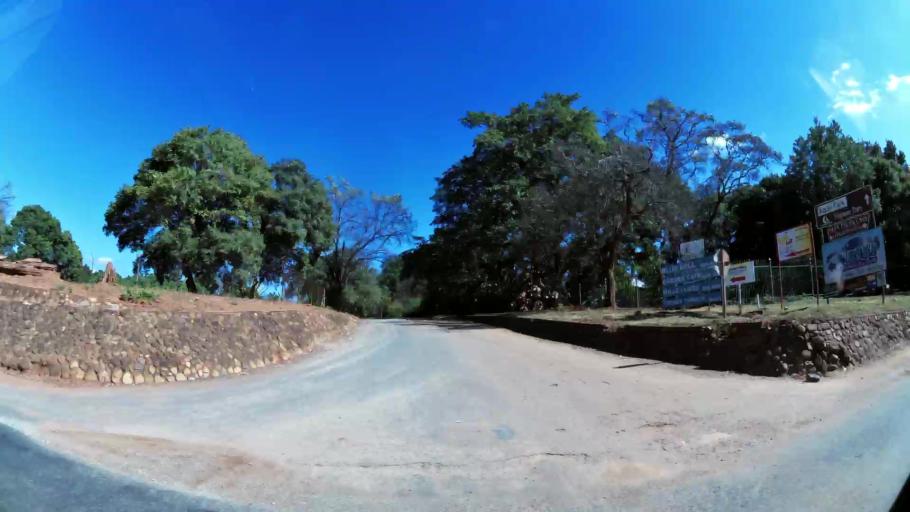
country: ZA
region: Limpopo
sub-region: Mopani District Municipality
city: Tzaneen
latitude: -23.8199
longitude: 30.1585
